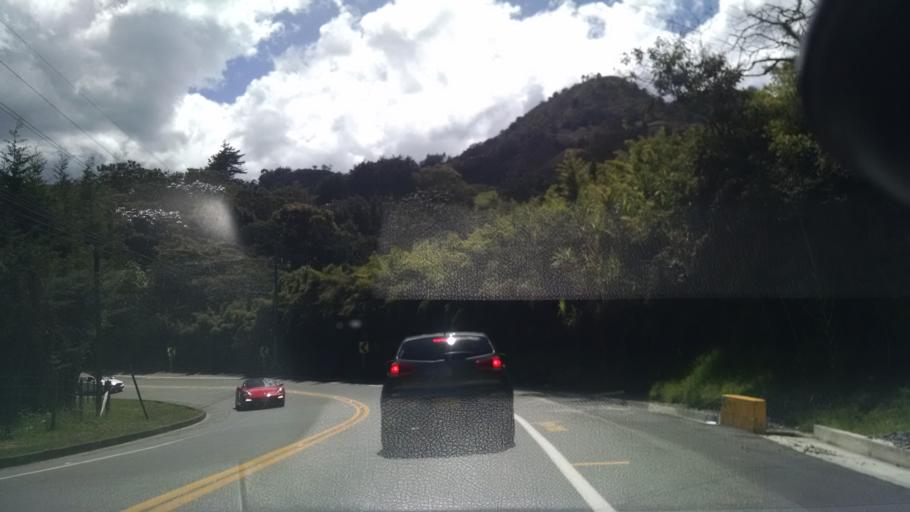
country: CO
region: Antioquia
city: El Retiro
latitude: 6.1208
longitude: -75.5010
